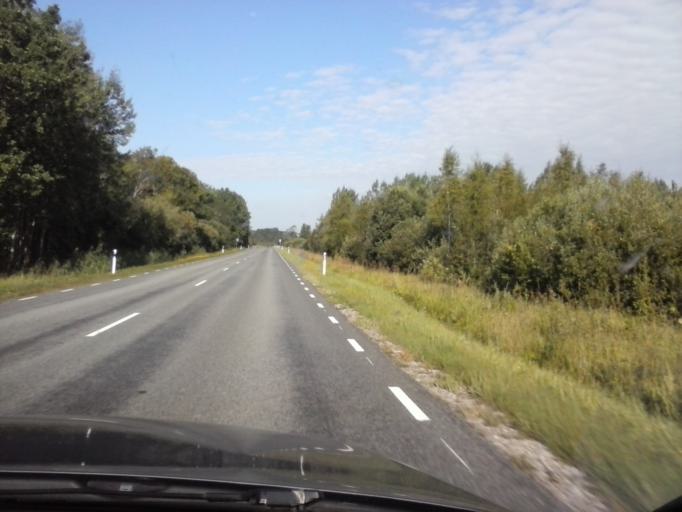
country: EE
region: Laeaene
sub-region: Lihula vald
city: Lihula
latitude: 58.6251
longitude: 23.8911
